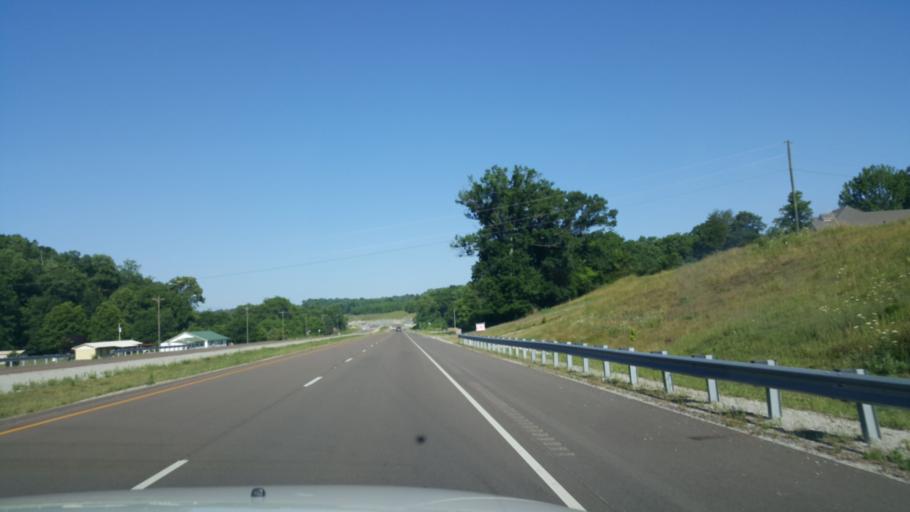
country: US
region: Tennessee
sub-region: Wayne County
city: Waynesboro
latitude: 35.2959
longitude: -87.8326
